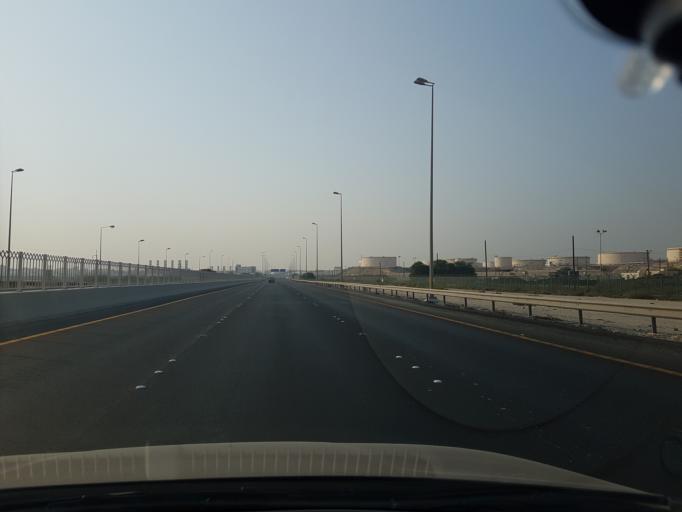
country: BH
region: Northern
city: Ar Rifa'
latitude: 26.1086
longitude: 50.5992
